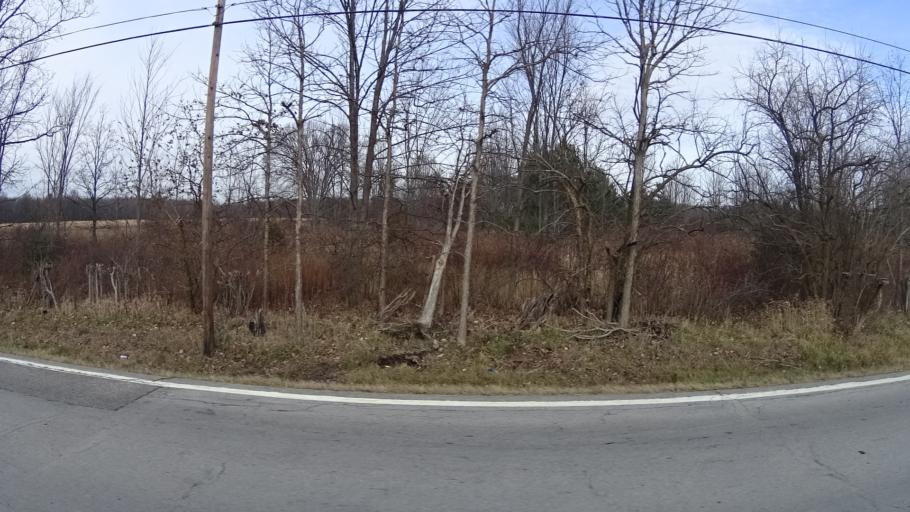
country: US
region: Ohio
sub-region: Lorain County
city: Eaton Estates
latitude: 41.2375
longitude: -81.9764
